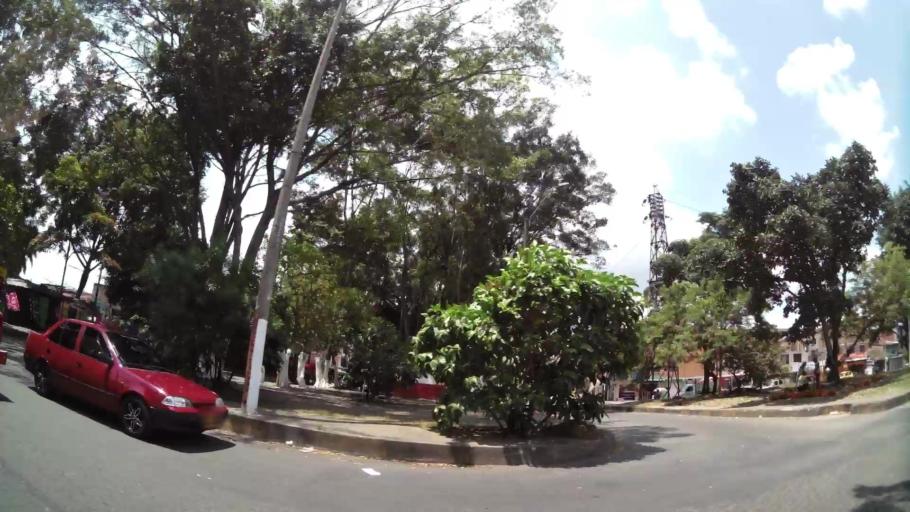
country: CO
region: Valle del Cauca
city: Cali
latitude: 3.4777
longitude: -76.4839
